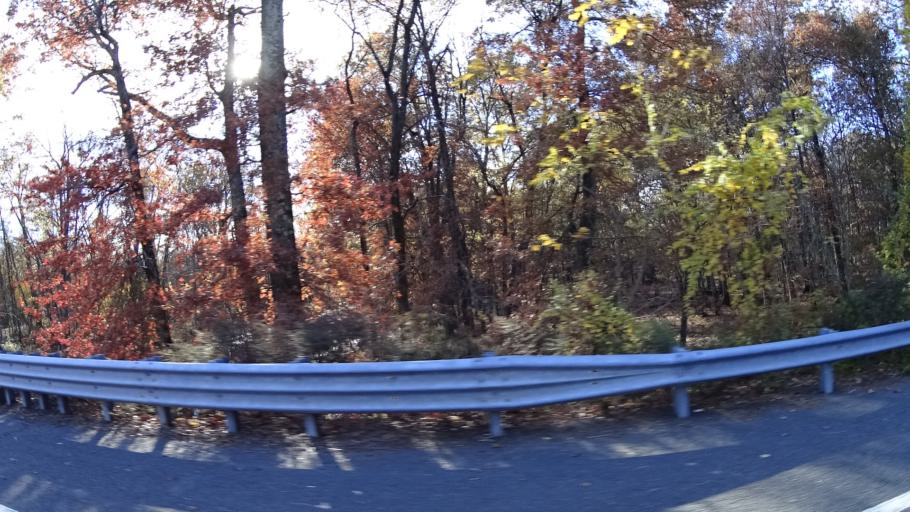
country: US
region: New Jersey
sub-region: Union County
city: Berkeley Heights
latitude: 40.6709
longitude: -74.4646
